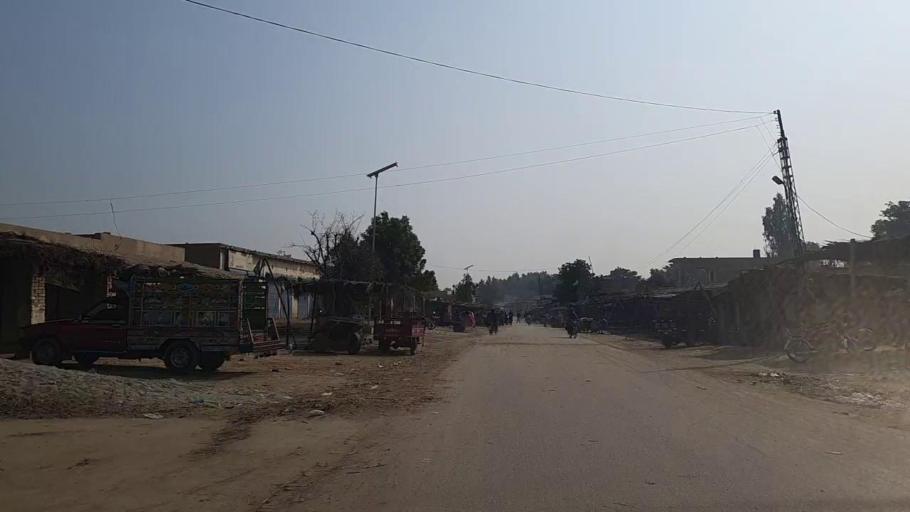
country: PK
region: Sindh
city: Jam Sahib
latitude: 26.3324
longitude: 68.5372
